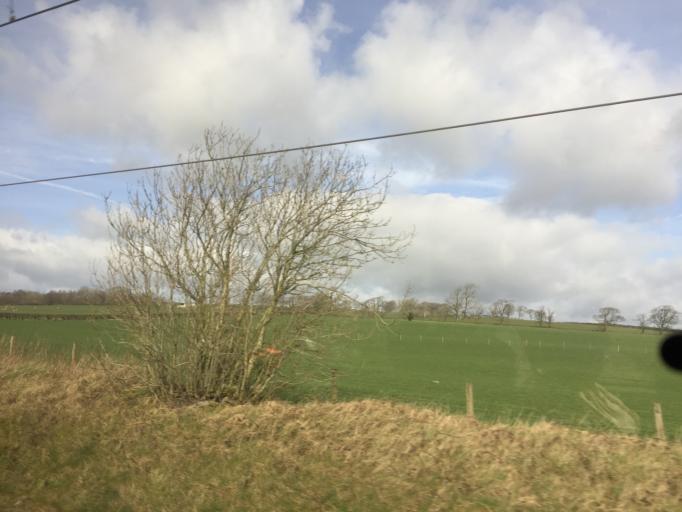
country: GB
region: Scotland
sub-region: Dumfries and Galloway
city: Annan
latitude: 55.0652
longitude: -3.2340
